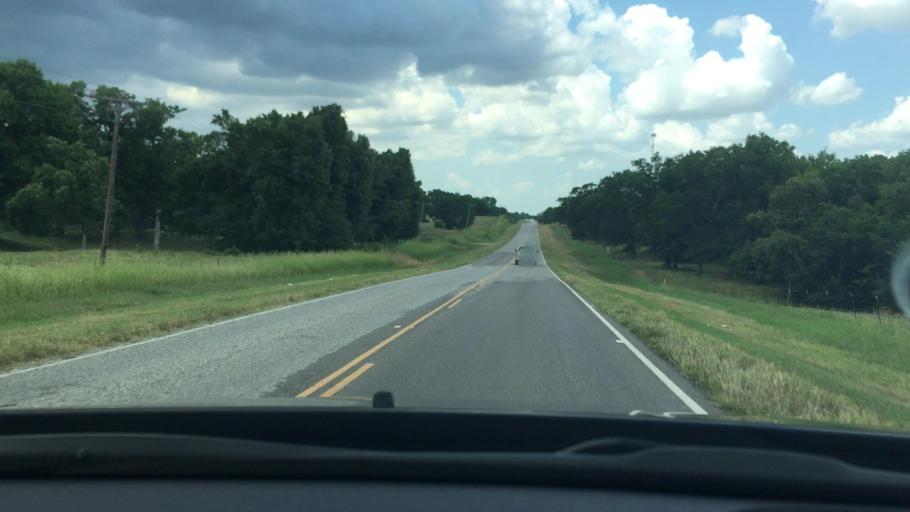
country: US
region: Oklahoma
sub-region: Pontotoc County
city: Ada
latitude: 34.5845
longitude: -96.6347
